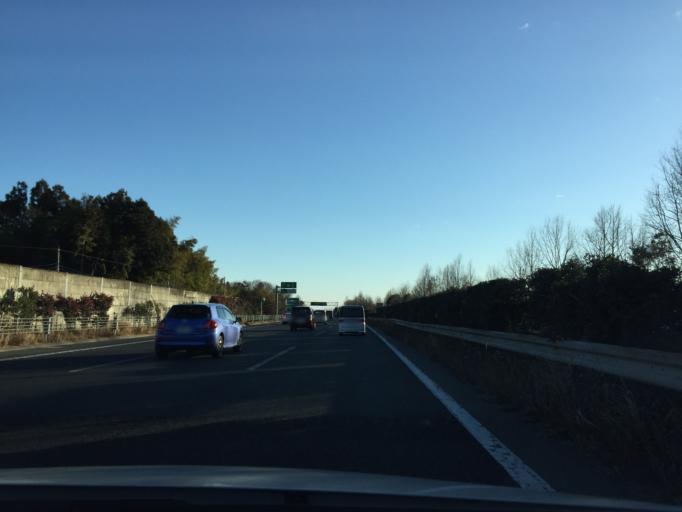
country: JP
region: Tochigi
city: Utsunomiya-shi
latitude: 36.6210
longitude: 139.8427
